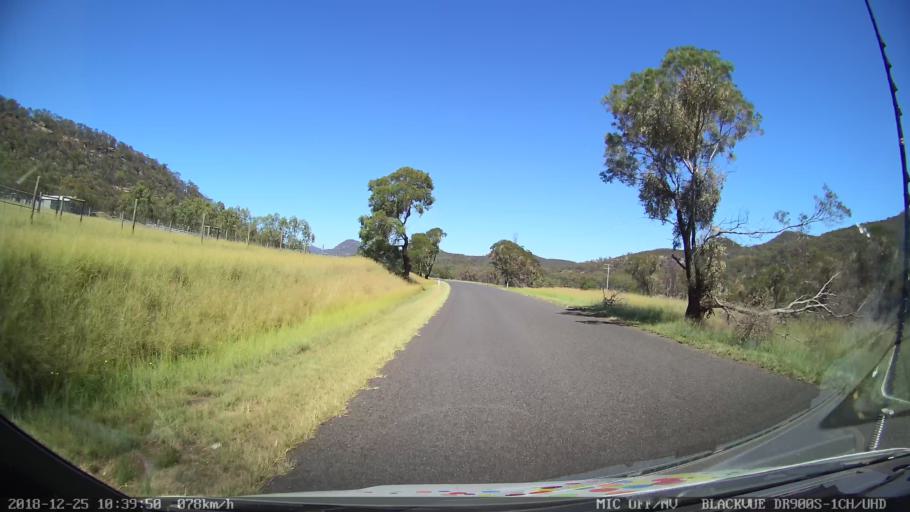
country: AU
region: New South Wales
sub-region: Upper Hunter Shire
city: Merriwa
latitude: -32.4047
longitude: 150.3507
